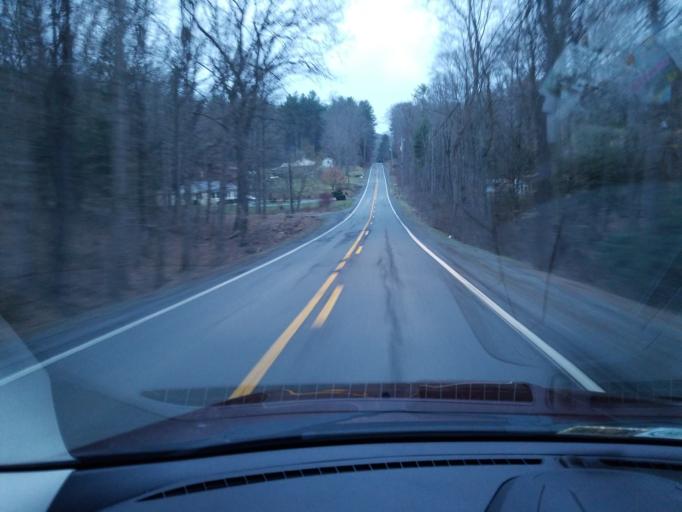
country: US
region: West Virginia
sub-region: Greenbrier County
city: Lewisburg
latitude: 37.7645
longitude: -80.3958
